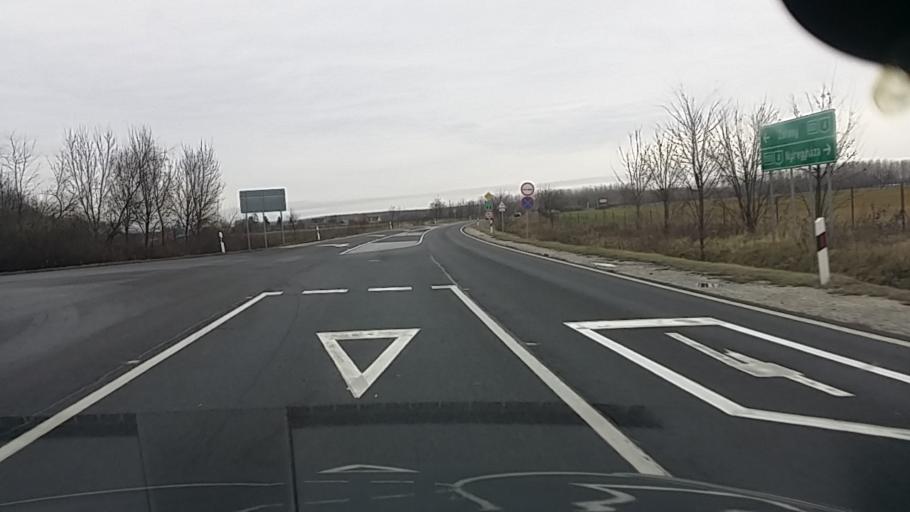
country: HU
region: Szabolcs-Szatmar-Bereg
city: Nyirbogdany
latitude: 48.0421
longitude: 21.8647
